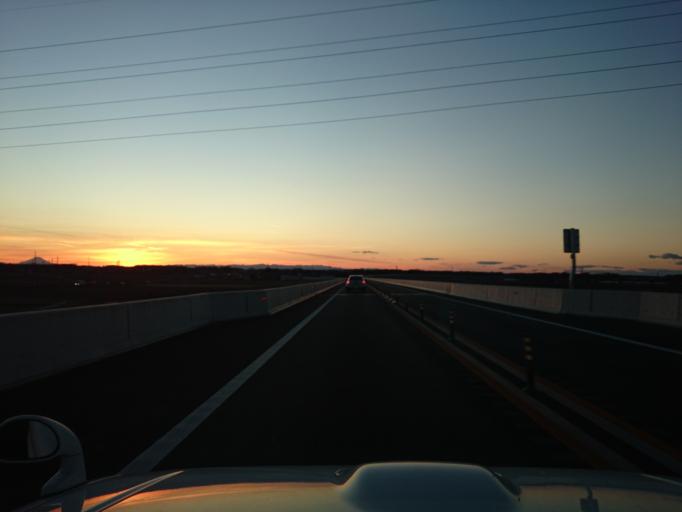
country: JP
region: Ibaraki
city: Iwai
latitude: 36.0712
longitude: 139.9408
